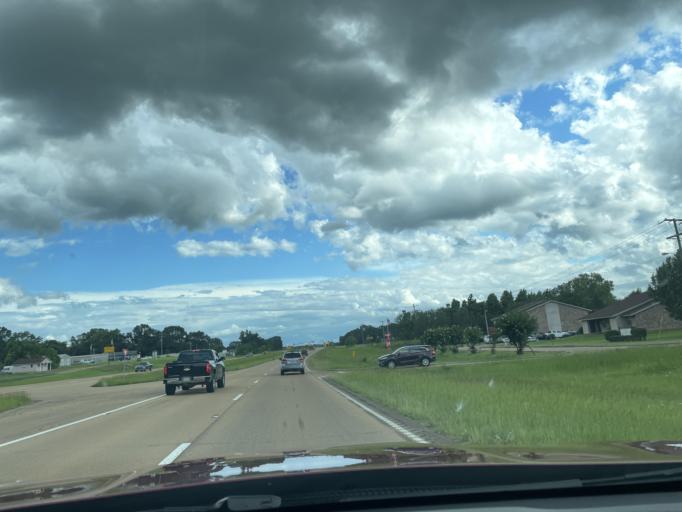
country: US
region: Mississippi
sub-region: Madison County
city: Flora
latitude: 32.5569
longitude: -90.3217
